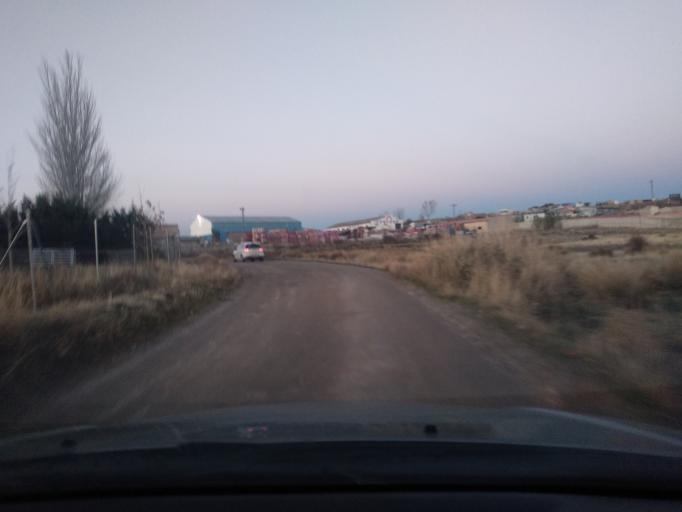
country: ES
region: Castille and Leon
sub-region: Provincia de Segovia
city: San Cristobal de Segovia
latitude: 40.9704
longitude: -4.0830
